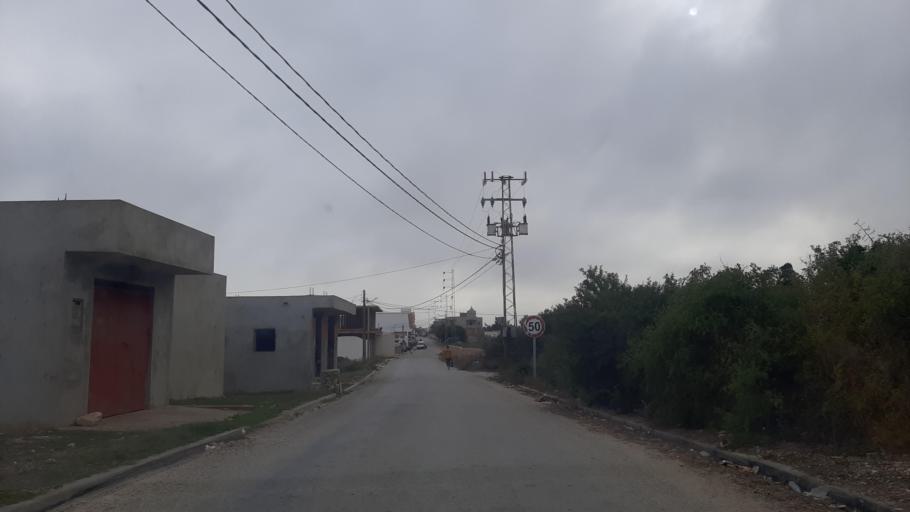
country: TN
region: Nabul
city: Menzel Heurr
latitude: 36.6822
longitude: 10.9268
